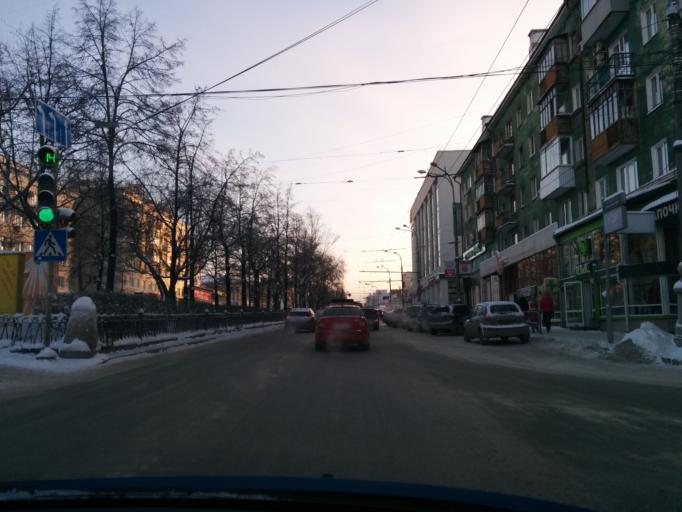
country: RU
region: Perm
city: Perm
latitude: 58.0127
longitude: 56.2373
